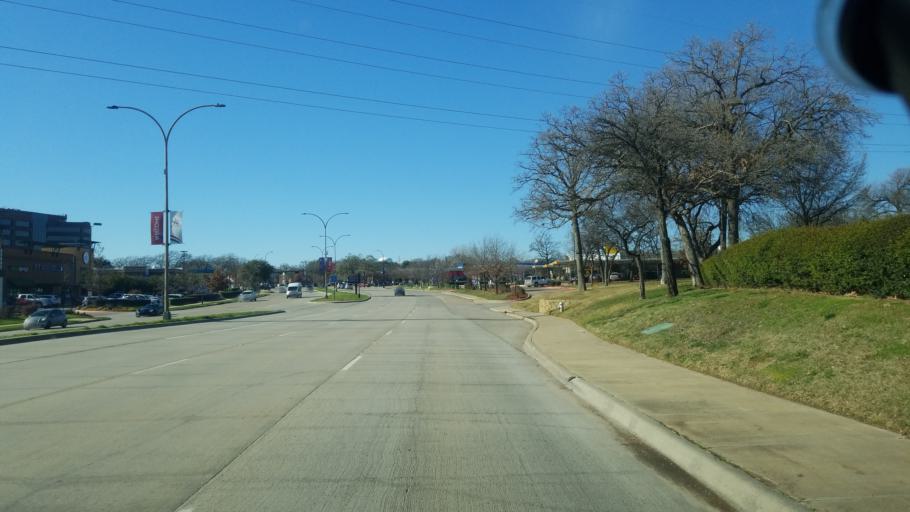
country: US
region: Texas
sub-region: Tarrant County
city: Arlington
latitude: 32.7619
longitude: -97.0729
